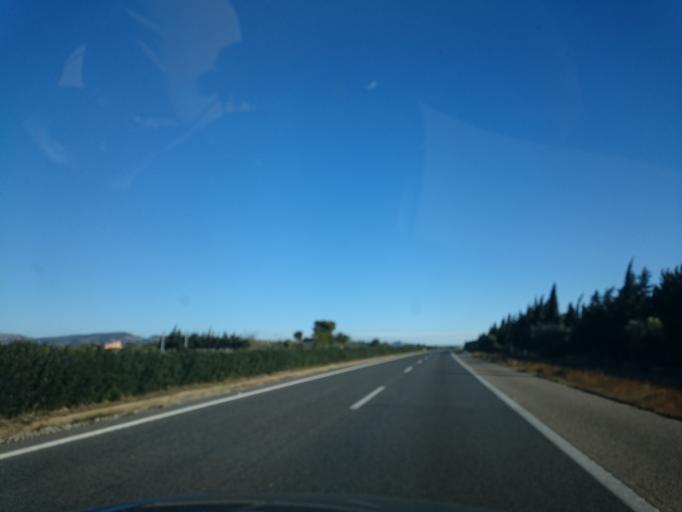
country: ES
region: Catalonia
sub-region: Provincia de Tarragona
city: Camarles
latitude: 40.7761
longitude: 0.6411
